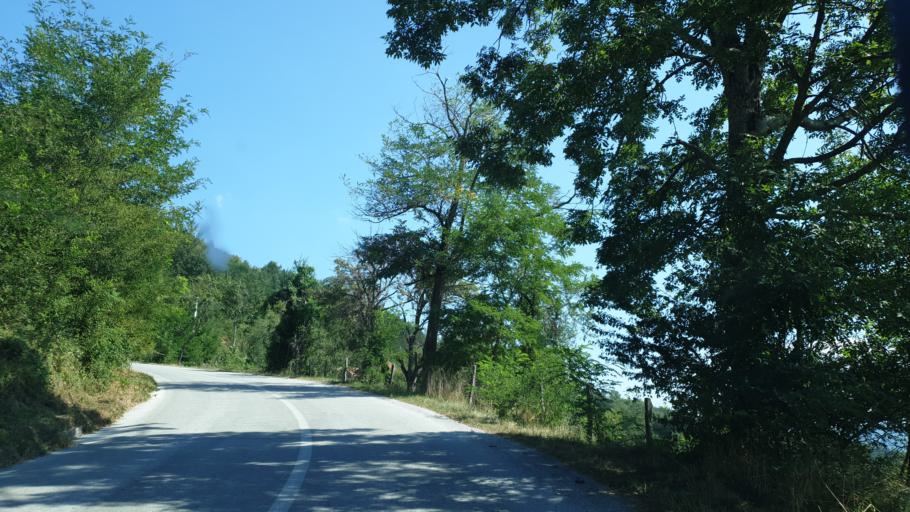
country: RS
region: Central Serbia
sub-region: Zlatiborski Okrug
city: Cajetina
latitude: 43.6770
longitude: 19.8286
